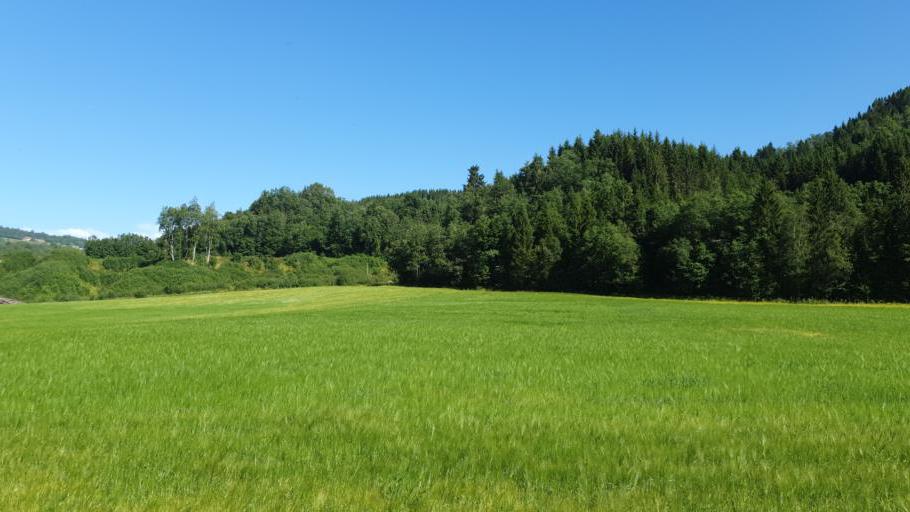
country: NO
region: Sor-Trondelag
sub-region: Orkdal
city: Orkanger
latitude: 63.1960
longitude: 9.7869
